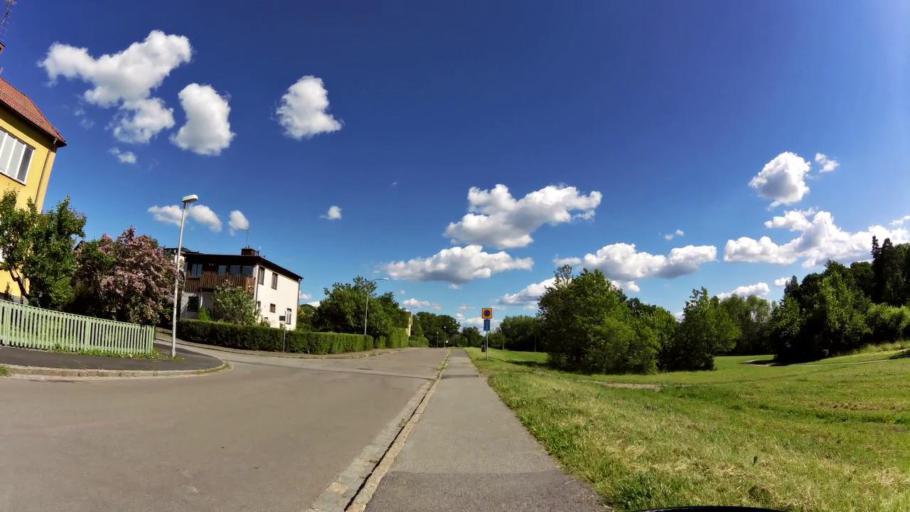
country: SE
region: OEstergoetland
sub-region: Linkopings Kommun
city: Linkoping
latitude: 58.3971
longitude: 15.6317
